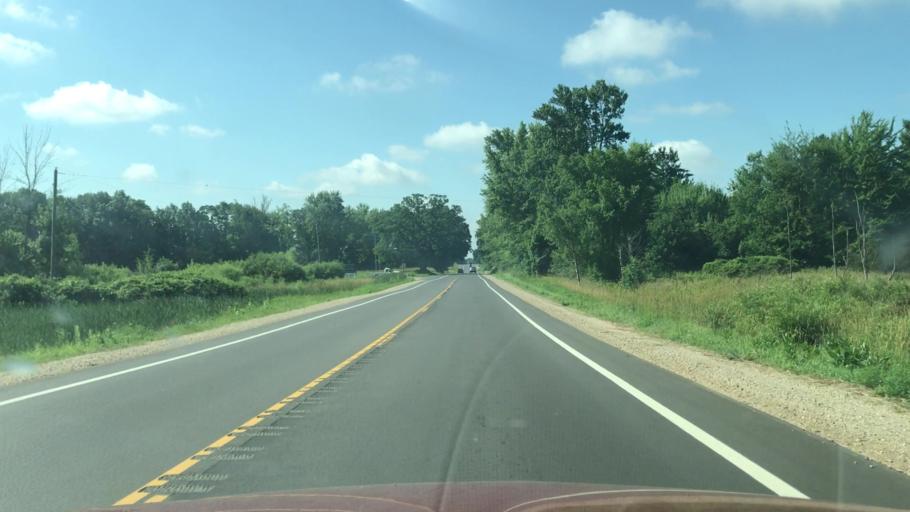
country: US
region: Michigan
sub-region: Newaygo County
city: Newaygo
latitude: 43.3790
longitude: -85.8009
